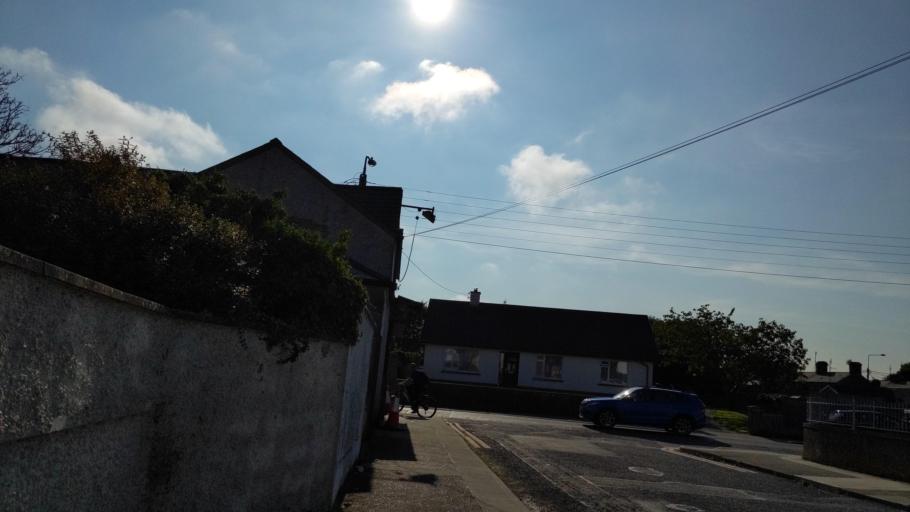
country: IE
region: Leinster
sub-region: Lu
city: Drogheda
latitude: 53.7086
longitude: -6.3486
